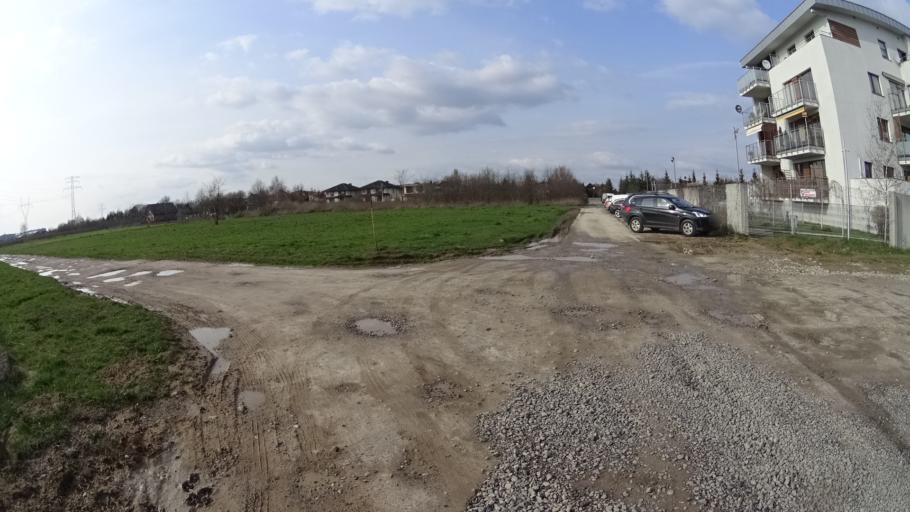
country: PL
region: Masovian Voivodeship
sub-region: Powiat warszawski zachodni
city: Babice
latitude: 52.2255
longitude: 20.8670
